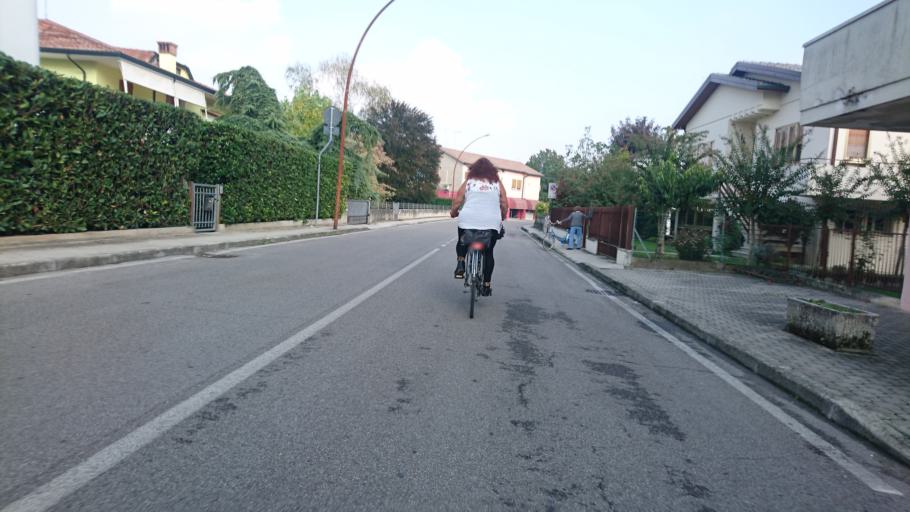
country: IT
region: Veneto
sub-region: Provincia di Rovigo
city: Polesella
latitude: 44.9635
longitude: 11.7514
